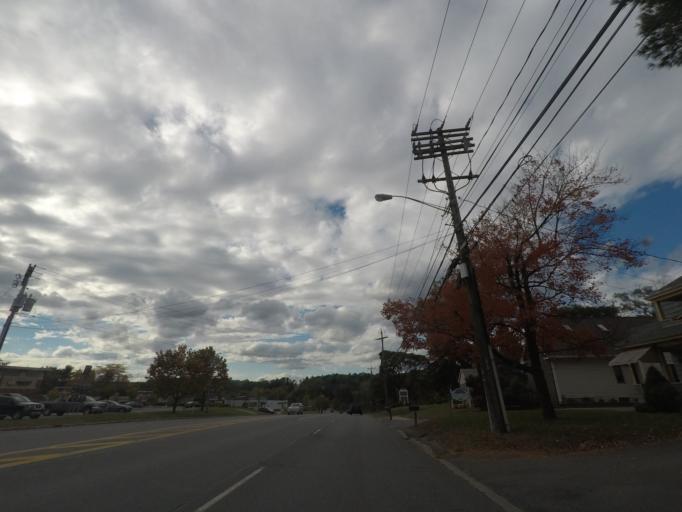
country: US
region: New York
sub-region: Albany County
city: Westmere
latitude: 42.6982
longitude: -73.8899
